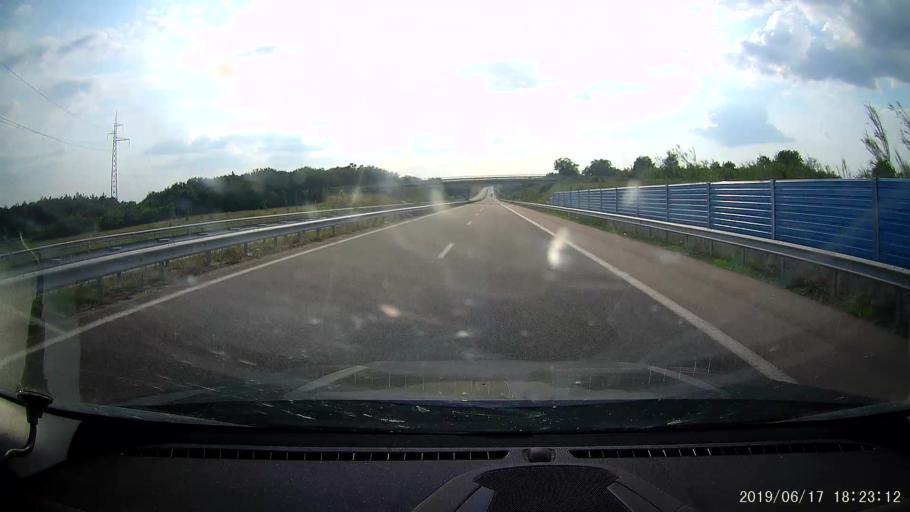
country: BG
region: Khaskovo
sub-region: Obshtina Simeonovgrad
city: Simeonovgrad
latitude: 41.9747
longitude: 25.7288
